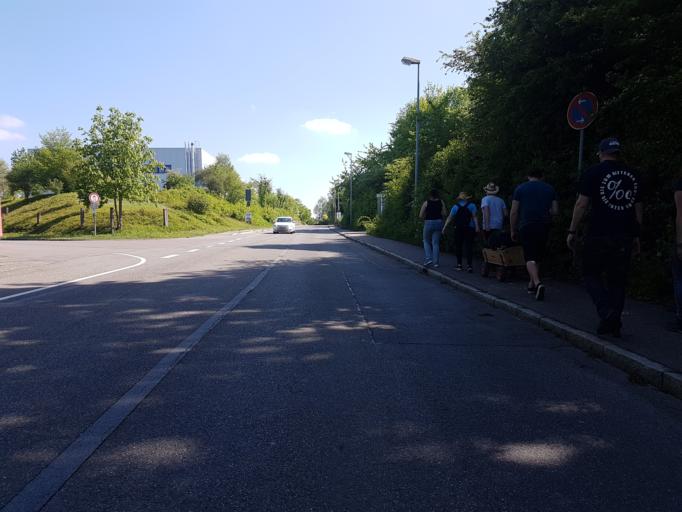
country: DE
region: Baden-Wuerttemberg
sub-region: Regierungsbezirk Stuttgart
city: Asperg
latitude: 48.9274
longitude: 9.1481
